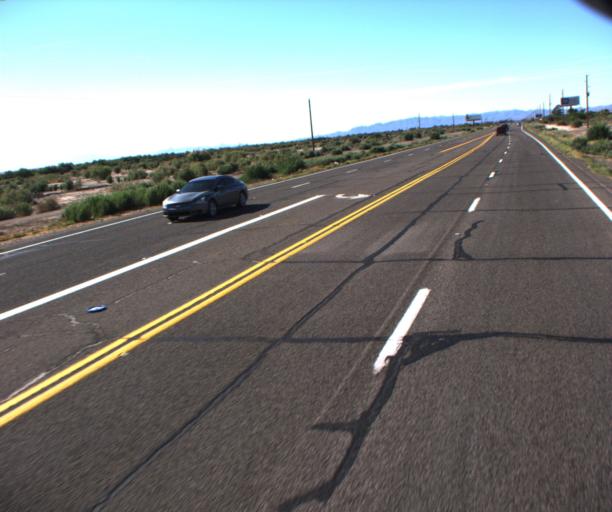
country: US
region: Arizona
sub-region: Mohave County
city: Mohave Valley
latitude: 34.9529
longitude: -114.5980
